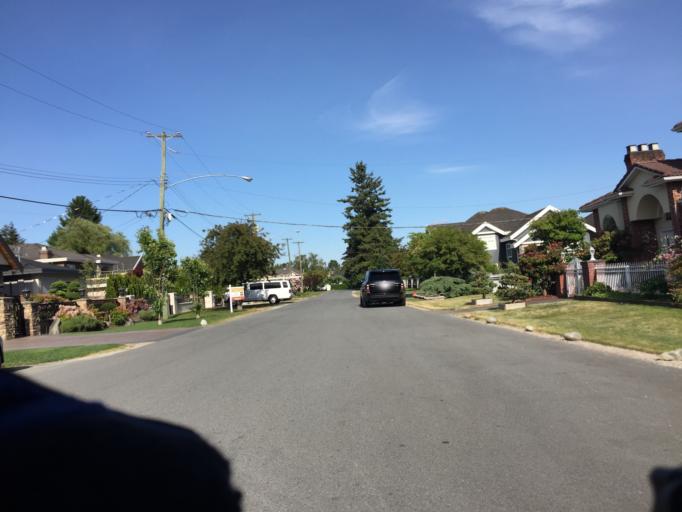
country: CA
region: British Columbia
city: Richmond
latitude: 49.1507
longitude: -123.1358
